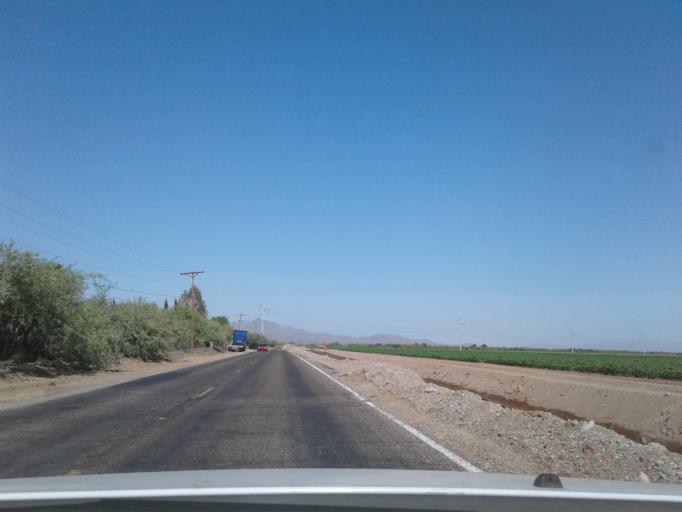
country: US
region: Arizona
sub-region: Maricopa County
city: Laveen
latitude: 33.3339
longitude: -112.1718
